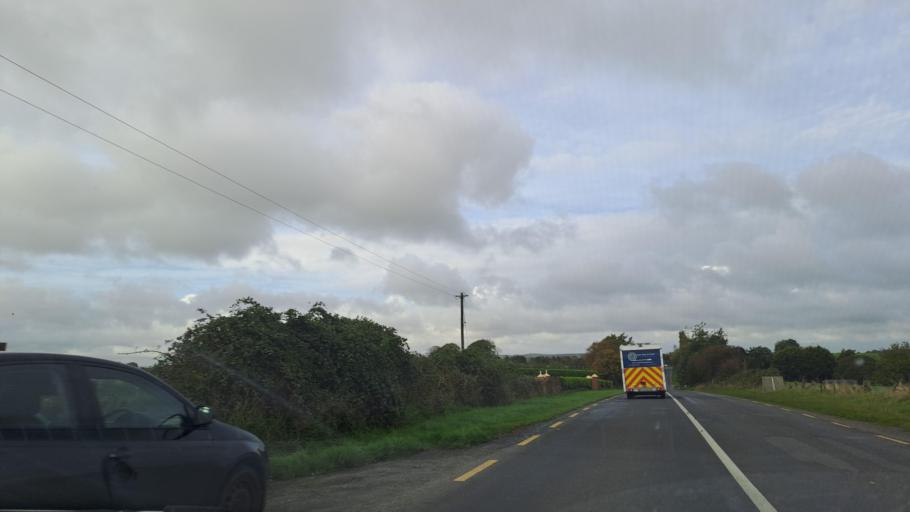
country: IE
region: Ulster
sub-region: An Cabhan
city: Kingscourt
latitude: 53.8018
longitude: -6.7373
